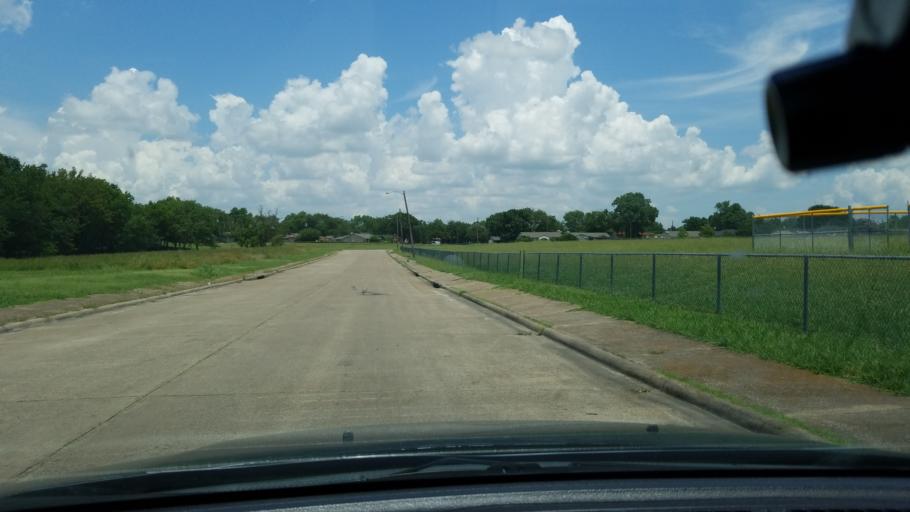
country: US
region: Texas
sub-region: Dallas County
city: Balch Springs
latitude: 32.7407
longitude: -96.6520
